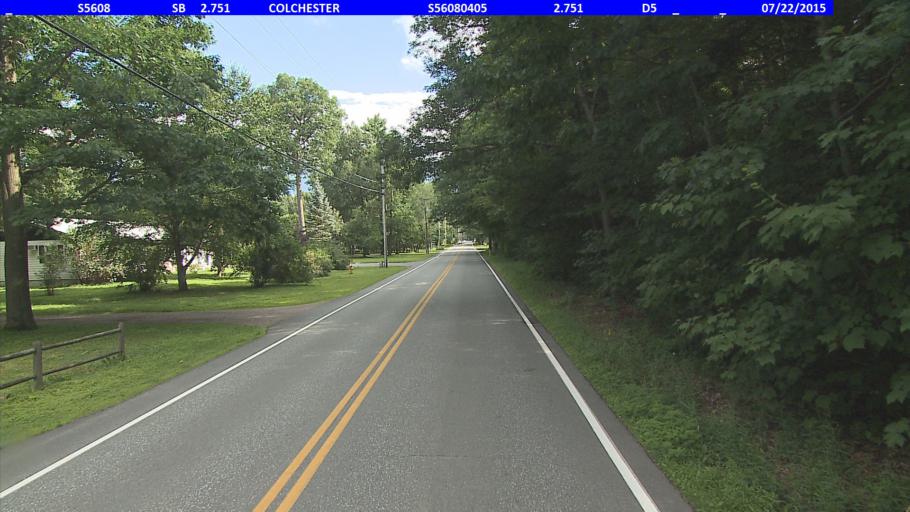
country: US
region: Vermont
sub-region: Chittenden County
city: Winooski
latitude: 44.5364
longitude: -73.2090
